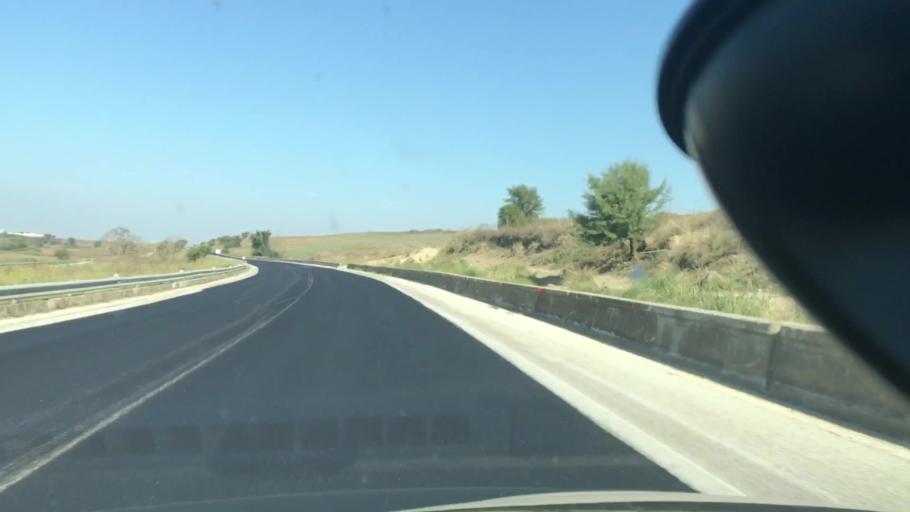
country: IT
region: Apulia
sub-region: Provincia di Barletta - Andria - Trani
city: Spinazzola
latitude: 40.9014
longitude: 16.1200
